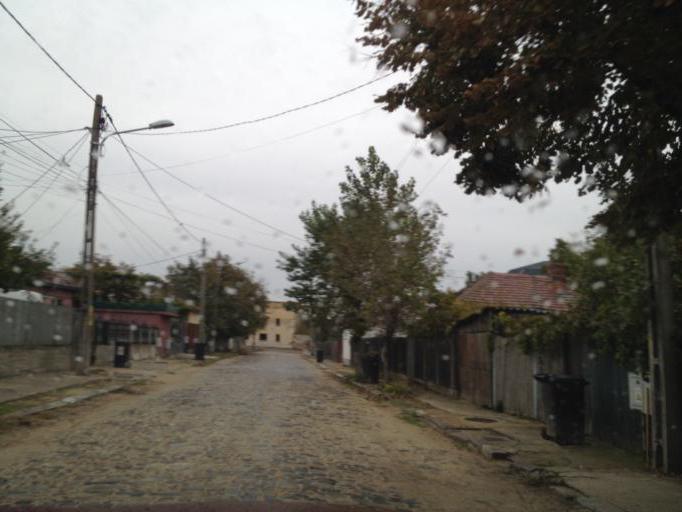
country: RO
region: Dolj
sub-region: Municipiul Craiova
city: Mofleni
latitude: 44.3131
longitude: 23.7750
